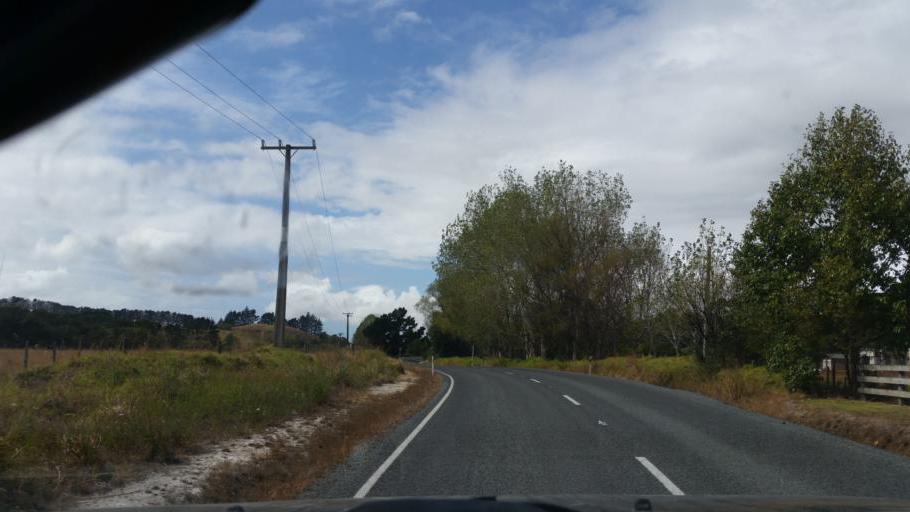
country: NZ
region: Auckland
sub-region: Auckland
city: Wellsford
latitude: -36.1217
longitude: 174.5525
